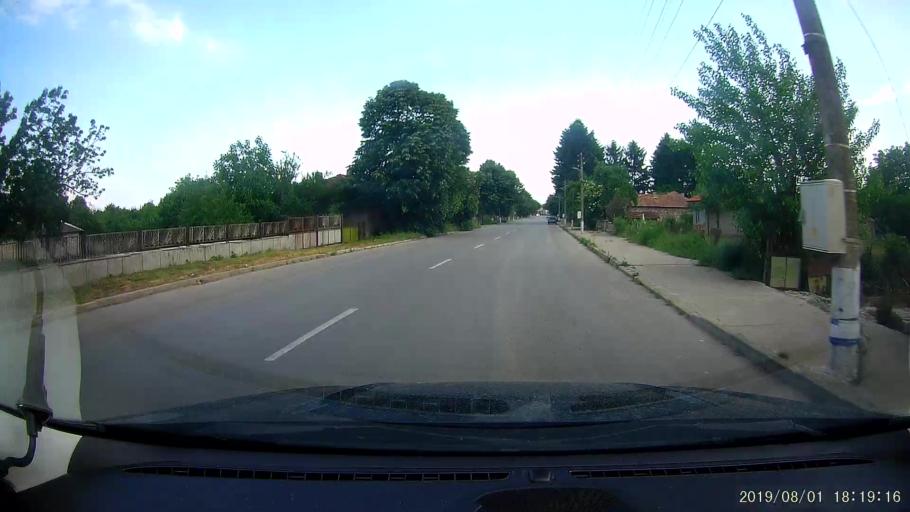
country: BG
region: Shumen
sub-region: Obshtina Kaolinovo
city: Kaolinovo
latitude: 43.6857
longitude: 27.0898
